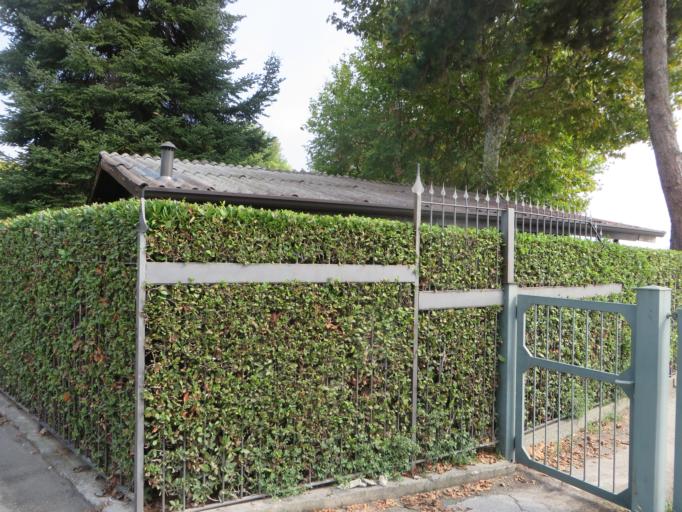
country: IT
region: Lombardy
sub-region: Provincia di Brescia
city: San Felice del Benaco
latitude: 45.5774
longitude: 10.5537
